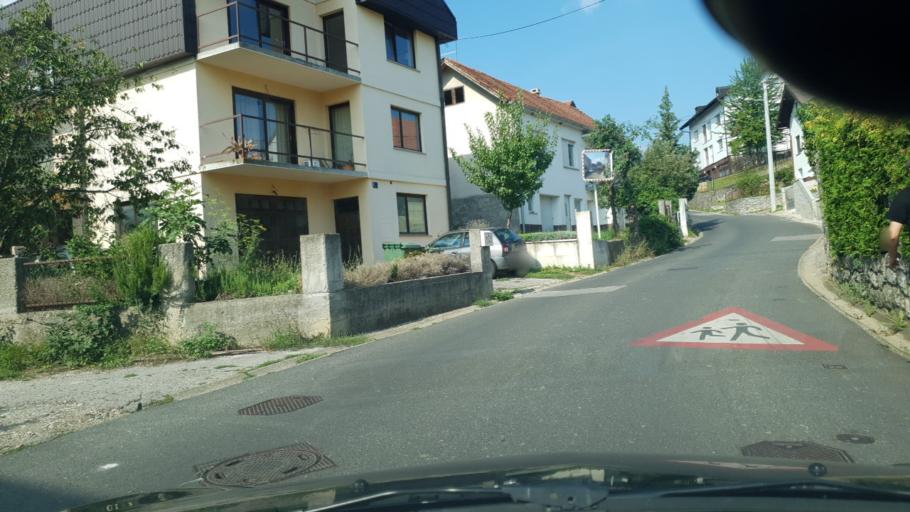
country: HR
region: Grad Zagreb
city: Zagreb
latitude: 45.8598
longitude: 15.9743
